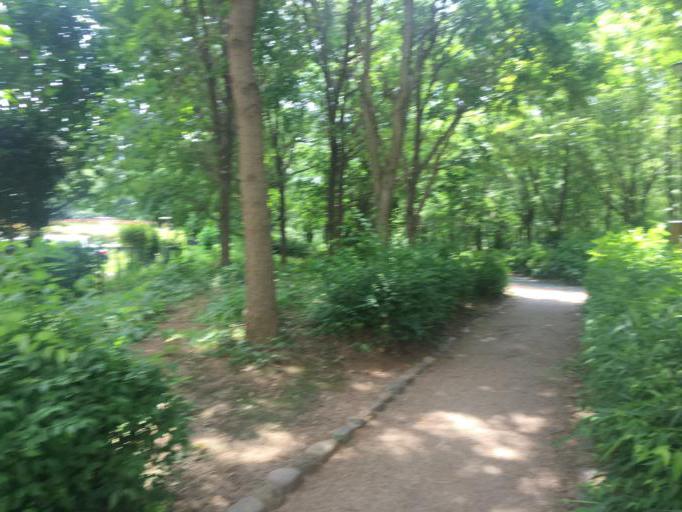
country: JP
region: Tokyo
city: Tanashicho
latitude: 35.7420
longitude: 139.5387
